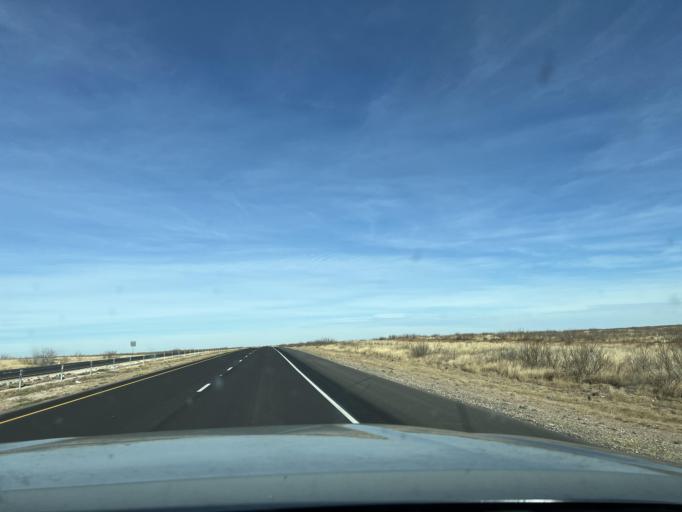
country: US
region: Texas
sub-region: Ector County
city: Gardendale
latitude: 32.0333
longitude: -102.4334
